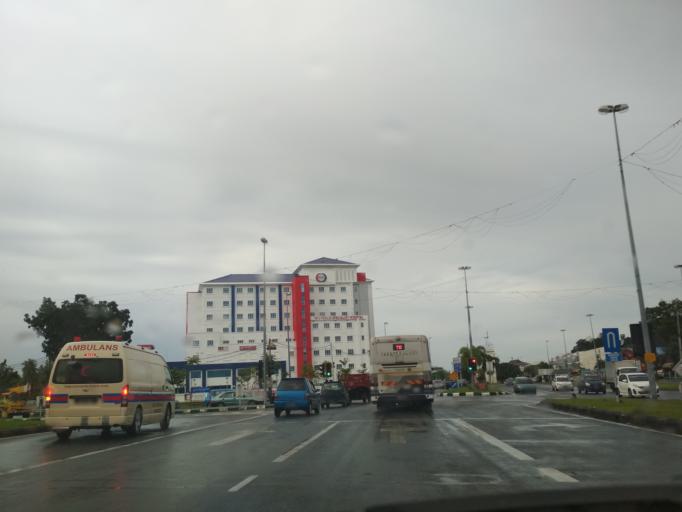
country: MY
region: Perlis
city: Kangar
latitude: 6.4313
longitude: 100.1856
